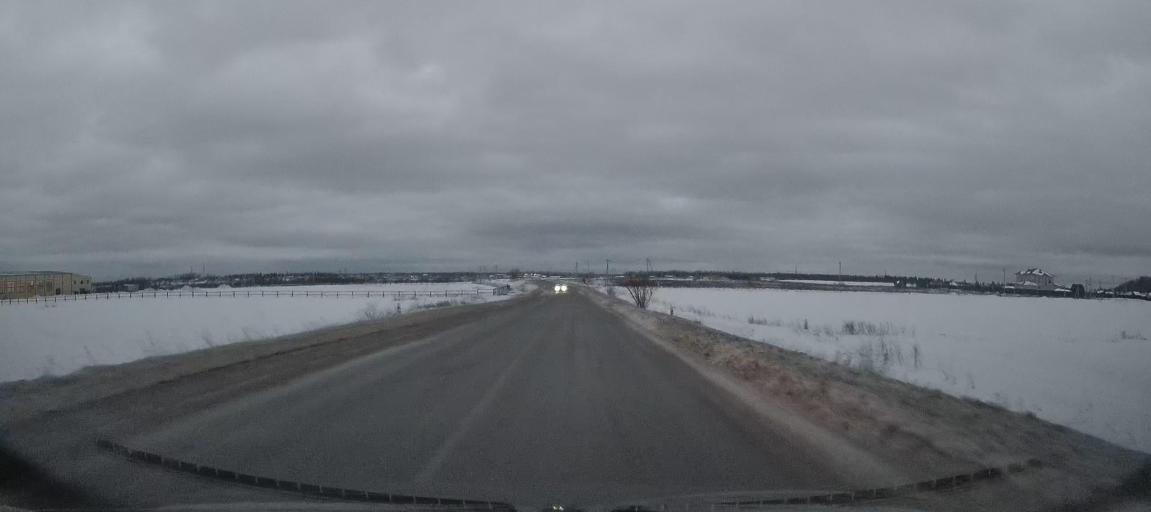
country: RU
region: Leningrad
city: Taytsy
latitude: 59.6908
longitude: 30.1397
